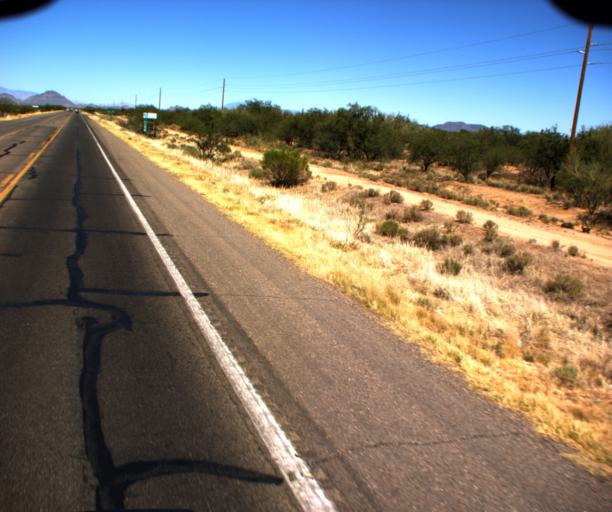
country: US
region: Arizona
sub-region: Pima County
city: Three Points
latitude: 32.1104
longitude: -111.2290
